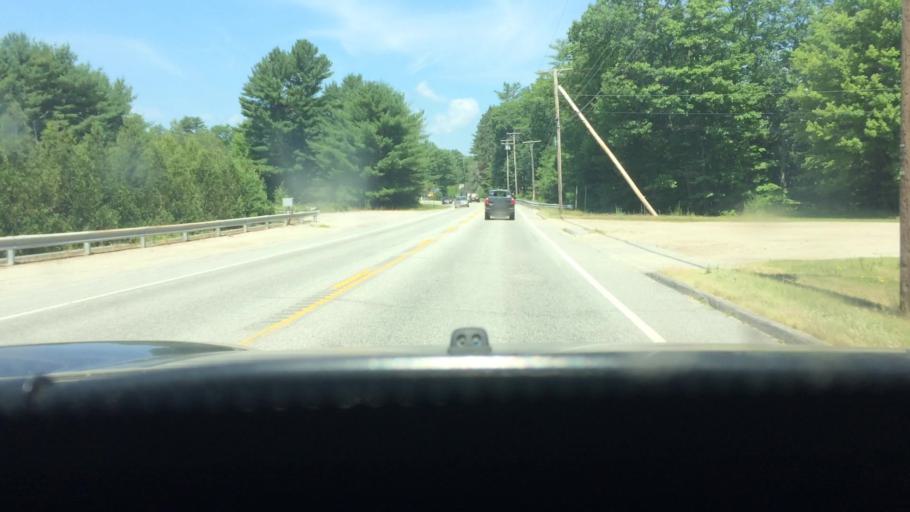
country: US
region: Maine
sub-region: Androscoggin County
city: Mechanic Falls
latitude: 44.1018
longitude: -70.3632
